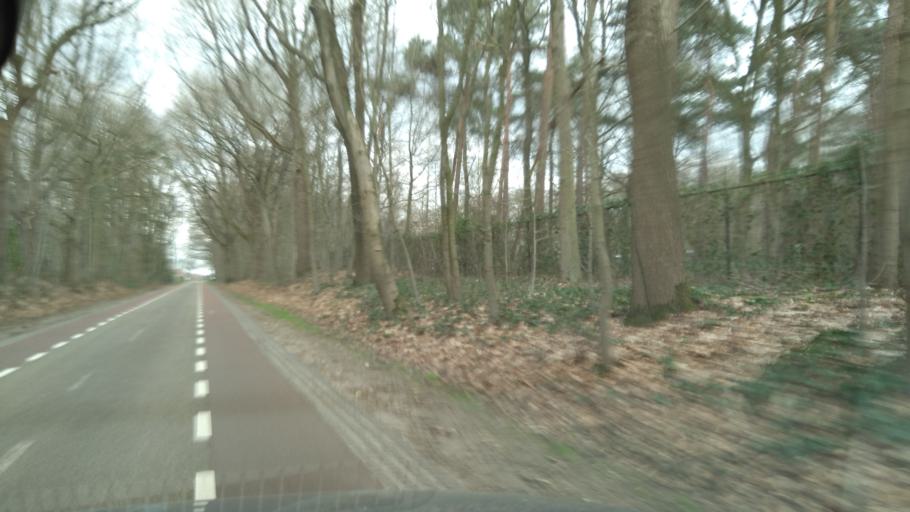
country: NL
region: North Brabant
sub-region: Gemeente Baarle-Nassau
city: Baarle-Nassau
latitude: 51.4291
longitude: 4.9589
